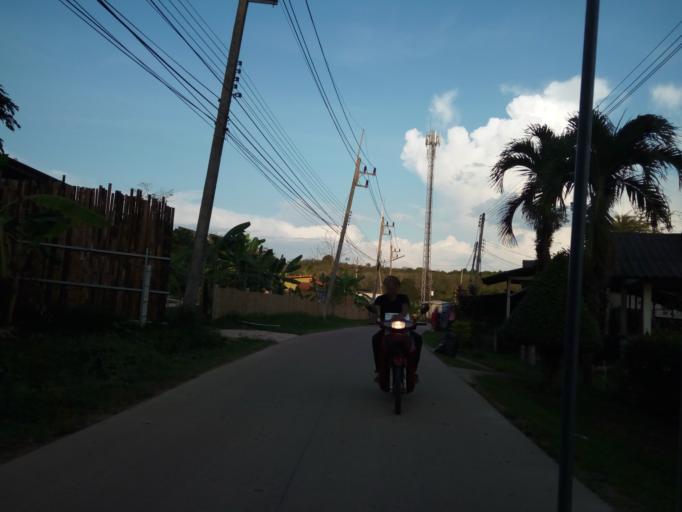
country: TH
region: Phangnga
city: Ko Yao
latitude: 8.0942
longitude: 98.6142
